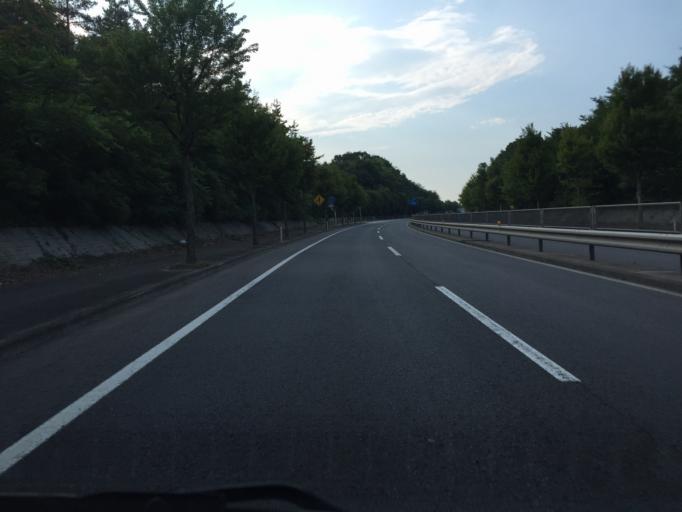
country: JP
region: Fukushima
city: Fukushima-shi
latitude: 37.6889
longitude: 140.4635
